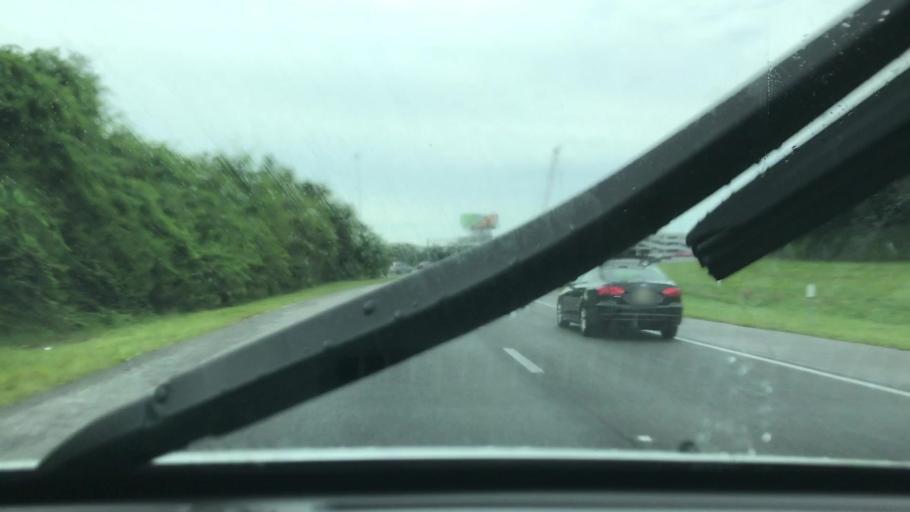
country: US
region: Florida
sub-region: Osceola County
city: Celebration
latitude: 28.3635
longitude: -81.5159
